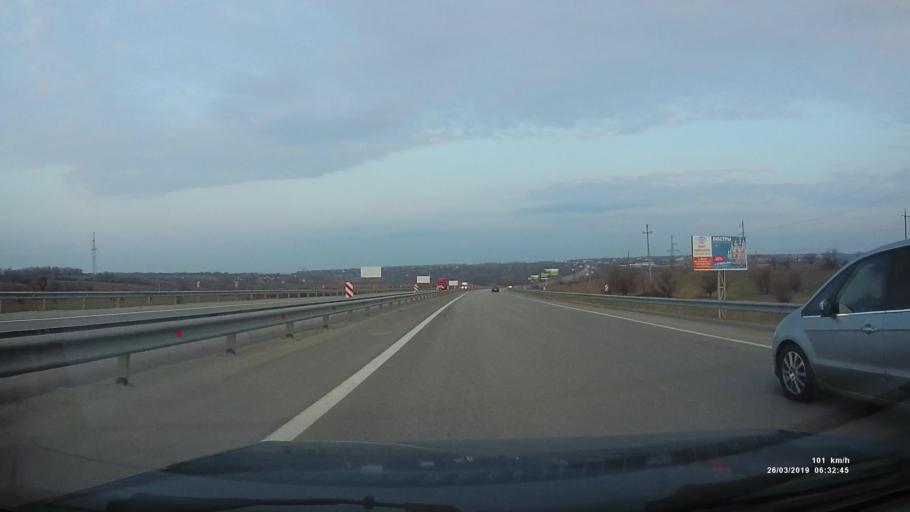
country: RU
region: Rostov
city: Kalinin
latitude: 47.2699
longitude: 39.5034
